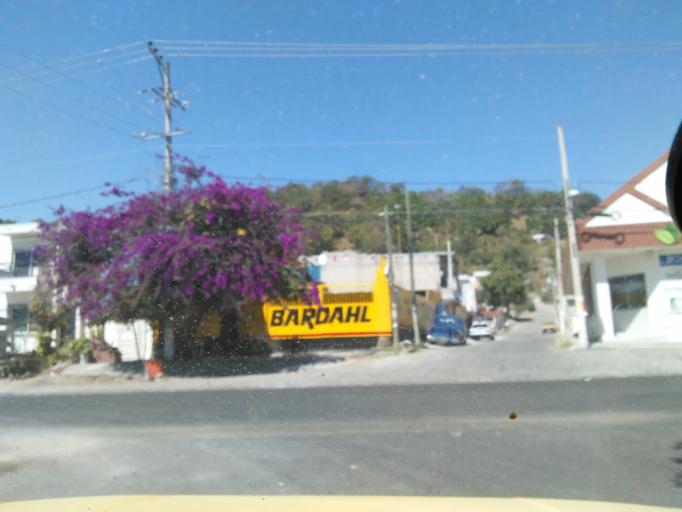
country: MX
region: Nayarit
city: Xalisco
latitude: 21.4386
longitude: -104.9001
